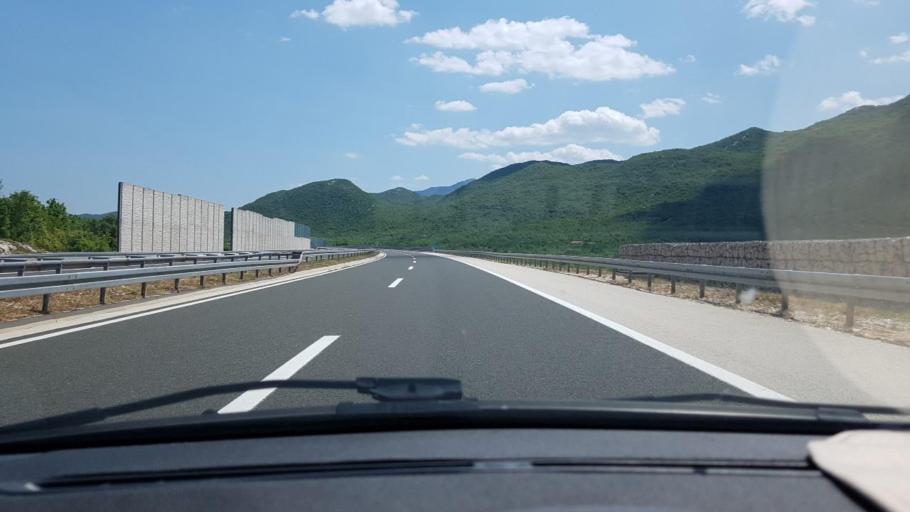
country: HR
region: Splitsko-Dalmatinska
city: Grubine
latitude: 43.3679
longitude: 17.0916
